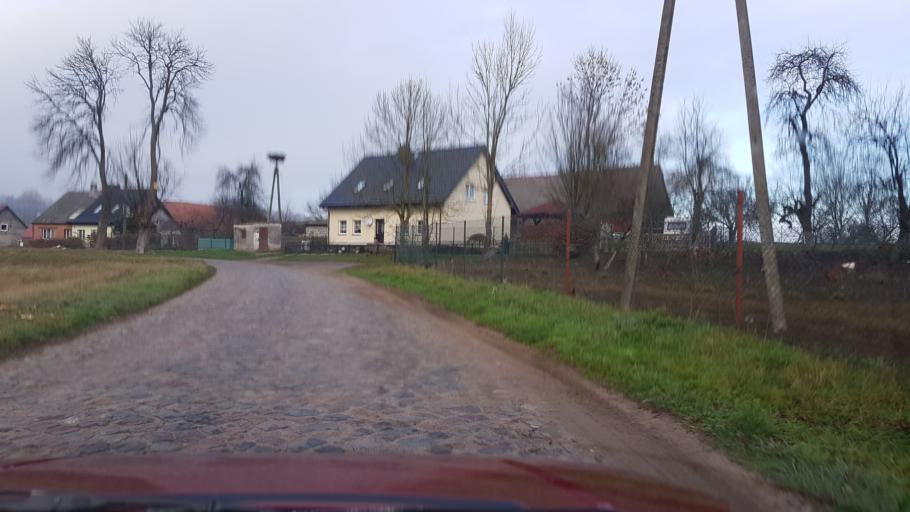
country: PL
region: West Pomeranian Voivodeship
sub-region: Powiat bialogardzki
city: Tychowo
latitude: 53.9783
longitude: 16.3151
